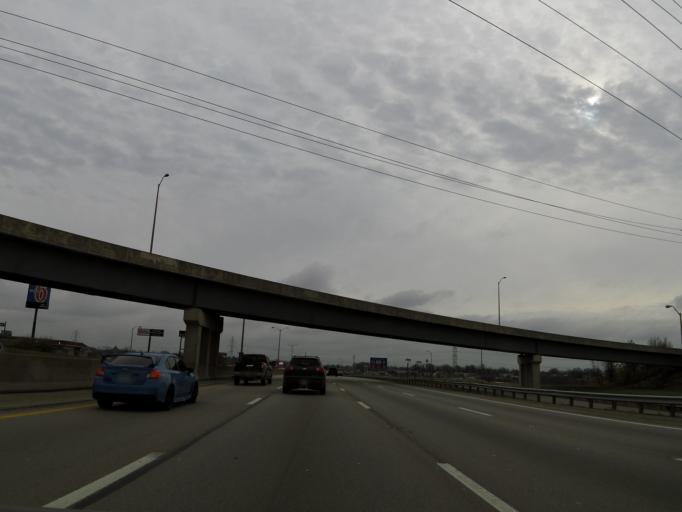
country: US
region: Kentucky
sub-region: Boone County
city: Florence
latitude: 38.9913
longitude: -84.6448
